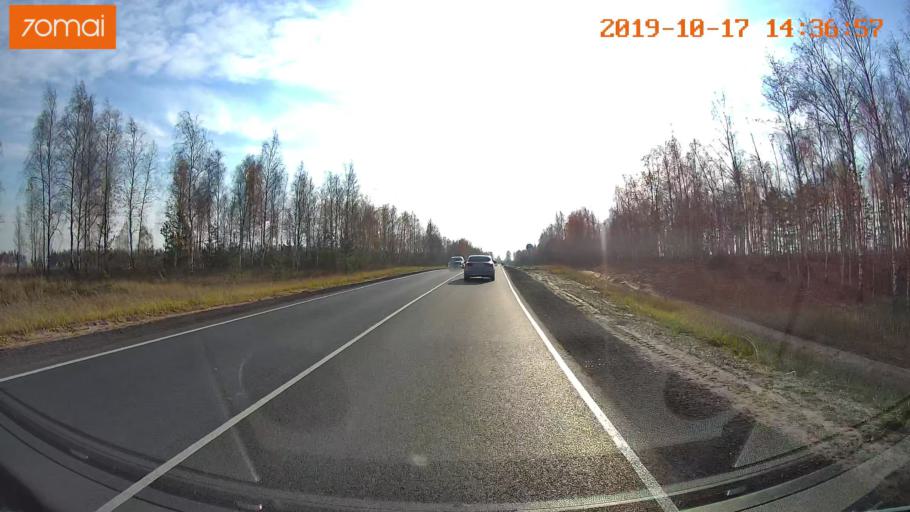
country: RU
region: Rjazan
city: Solotcha
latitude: 54.8845
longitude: 40.0005
